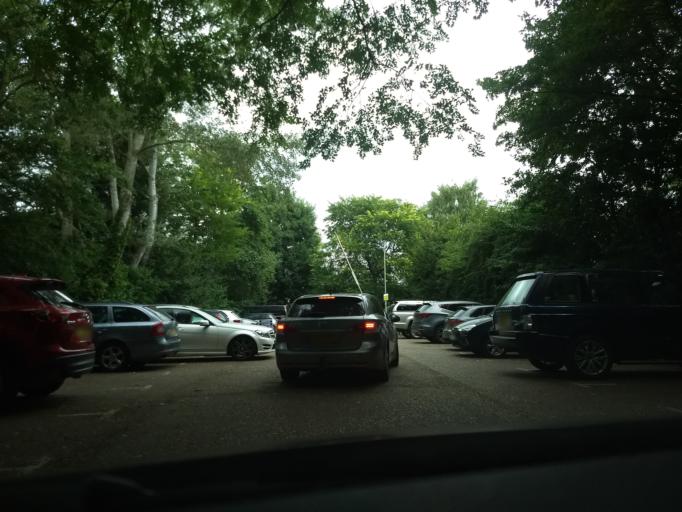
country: GB
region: England
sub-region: Suffolk
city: Shotley Gate
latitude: 51.9953
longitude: 1.2115
